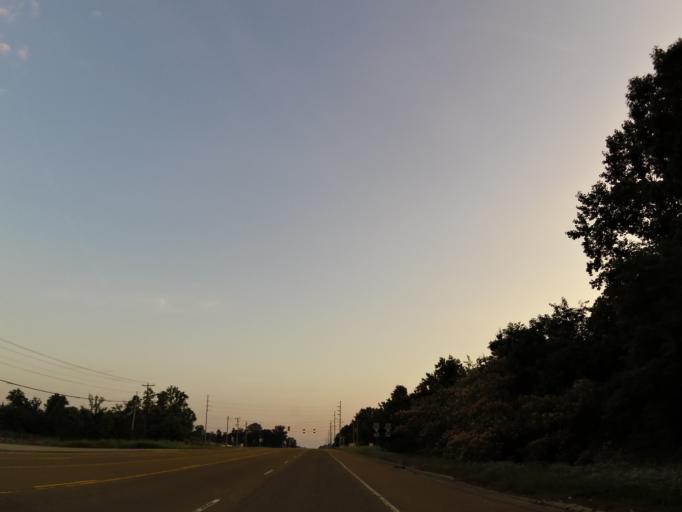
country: US
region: Tennessee
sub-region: Henry County
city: Paris
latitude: 36.2717
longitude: -88.3330
